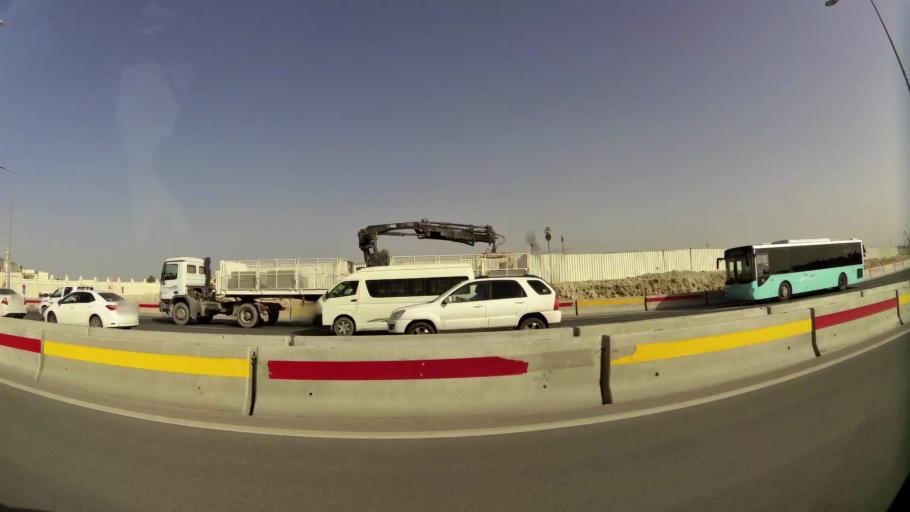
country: QA
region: Baladiyat ar Rayyan
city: Ar Rayyan
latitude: 25.3291
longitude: 51.4480
